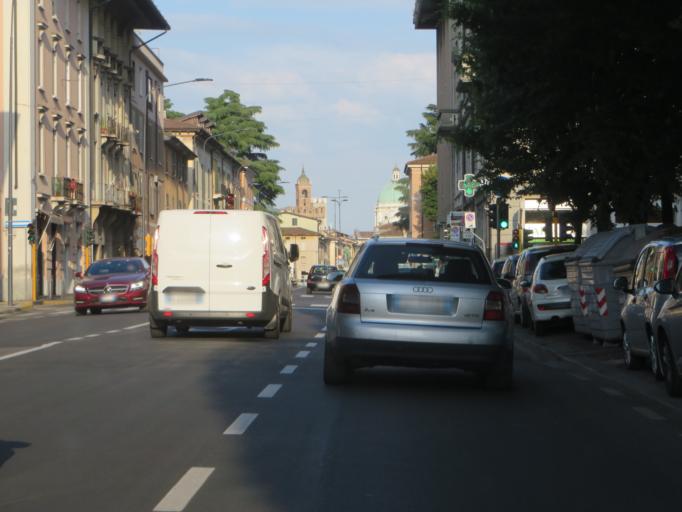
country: IT
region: Lombardy
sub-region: Provincia di Brescia
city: Brescia
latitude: 45.5427
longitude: 10.2074
